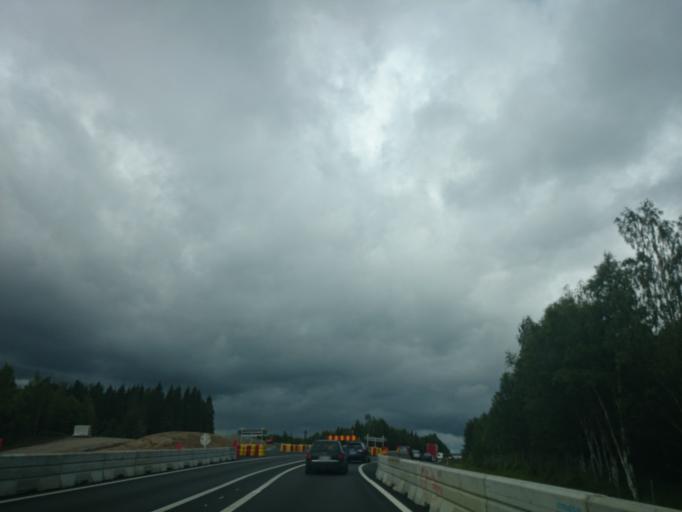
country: SE
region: Vaesternorrland
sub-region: Sundsvalls Kommun
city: Njurundabommen
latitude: 62.2525
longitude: 17.3713
